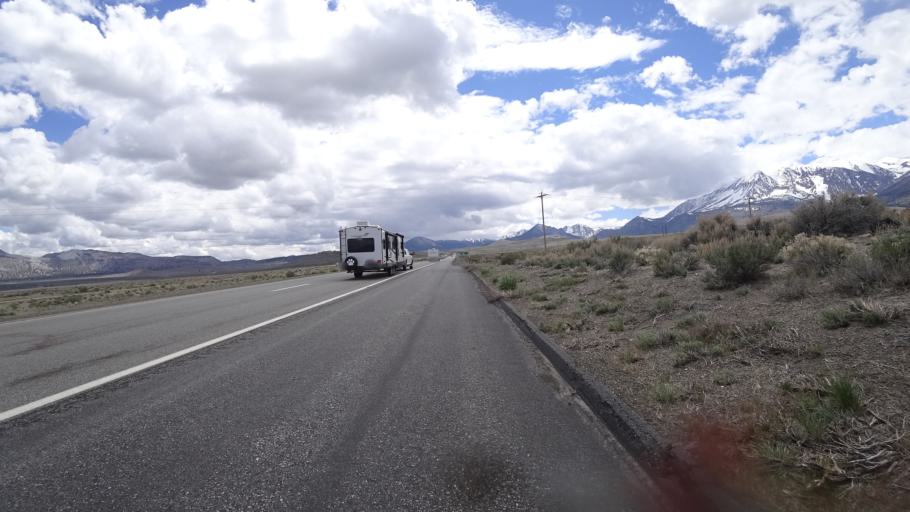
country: US
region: California
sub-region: Mono County
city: Mammoth Lakes
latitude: 37.8866
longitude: -119.0914
